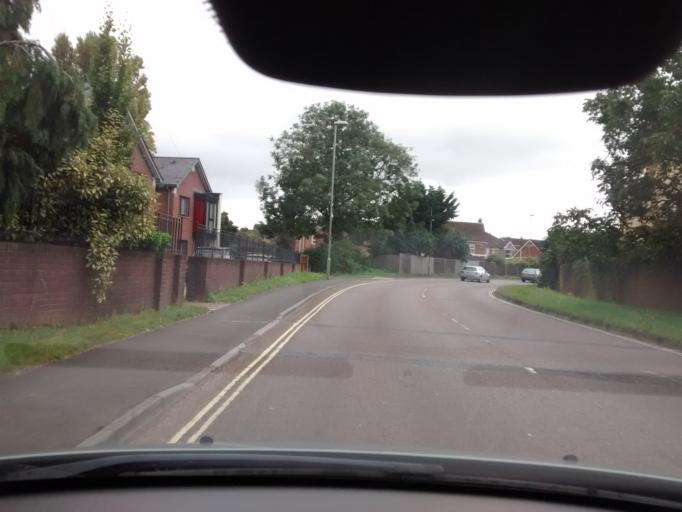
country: GB
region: England
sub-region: Hampshire
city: Ringwood
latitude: 50.8467
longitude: -1.7892
